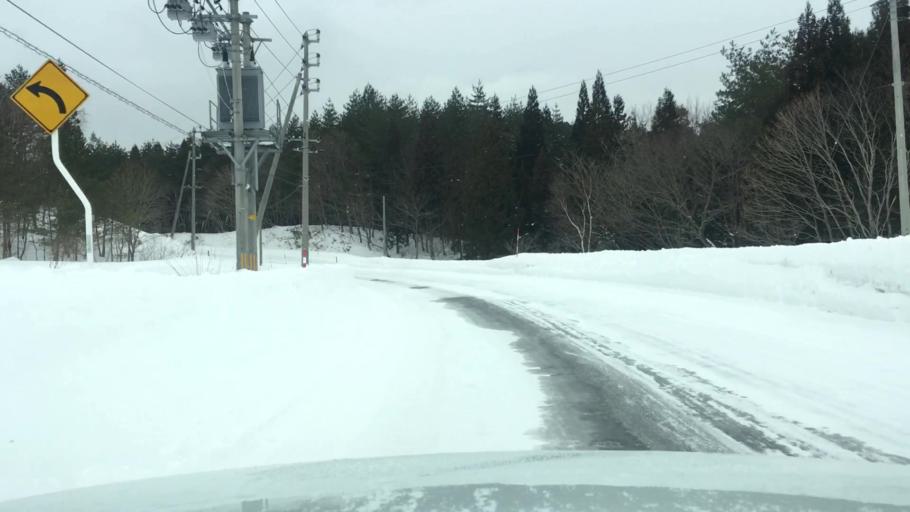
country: JP
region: Akita
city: Hanawa
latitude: 39.9940
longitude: 140.9954
